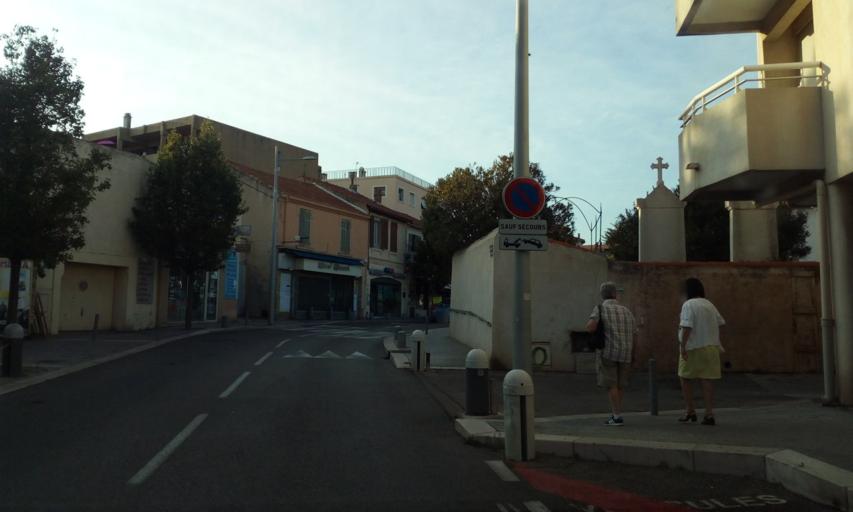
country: FR
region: Provence-Alpes-Cote d'Azur
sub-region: Departement du Var
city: Bandol
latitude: 43.1367
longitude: 5.7527
